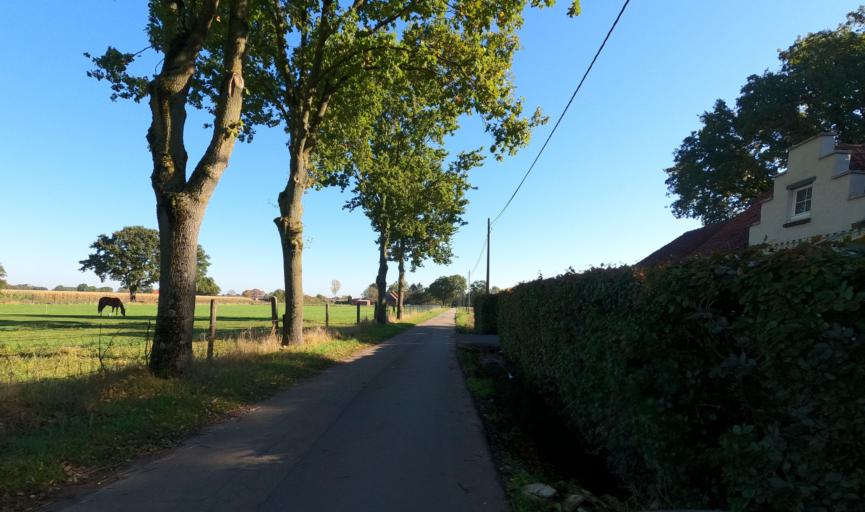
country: BE
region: Flanders
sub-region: Provincie Antwerpen
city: Herenthout
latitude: 51.1033
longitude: 4.7600
